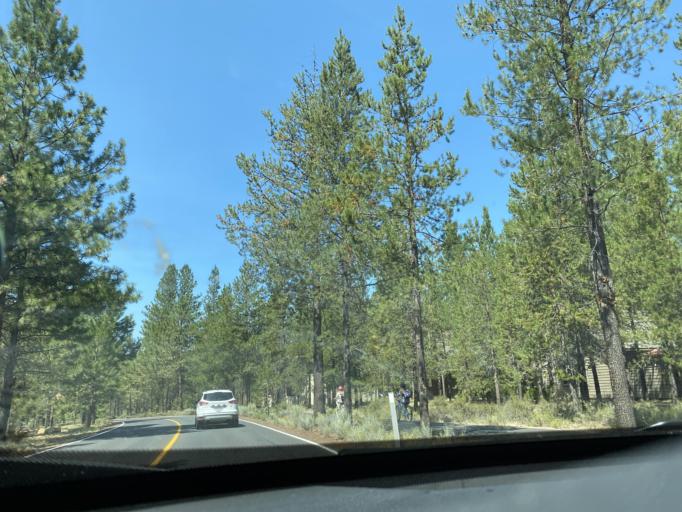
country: US
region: Oregon
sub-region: Deschutes County
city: Sunriver
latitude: 43.8890
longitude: -121.4329
